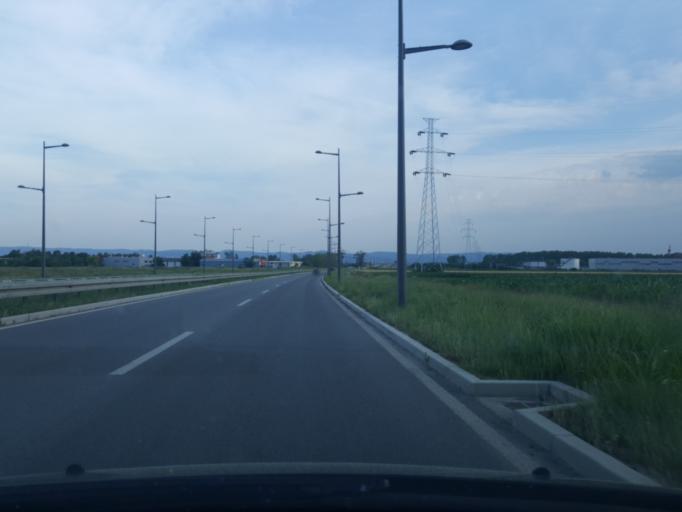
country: RS
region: Autonomna Pokrajina Vojvodina
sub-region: Juznobacki Okrug
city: Novi Sad
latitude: 45.2936
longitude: 19.8076
